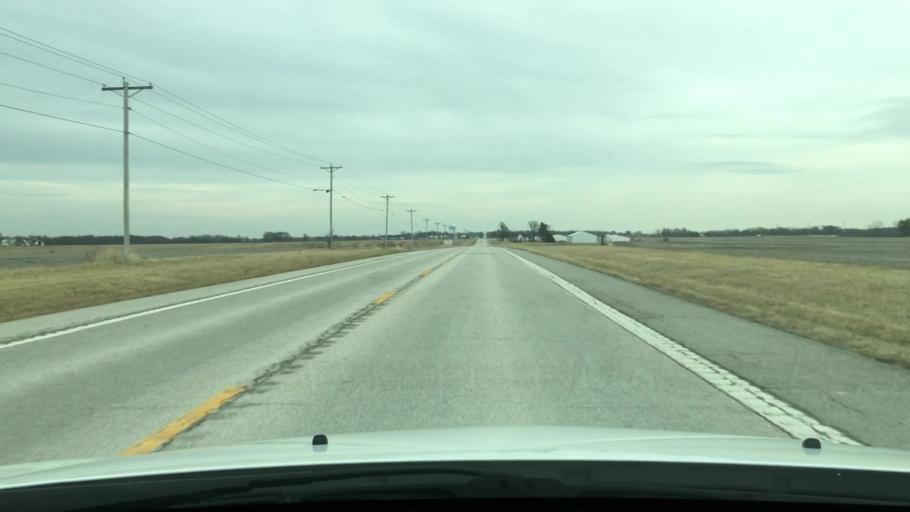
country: US
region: Missouri
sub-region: Audrain County
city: Vandalia
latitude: 39.3460
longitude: -91.3746
